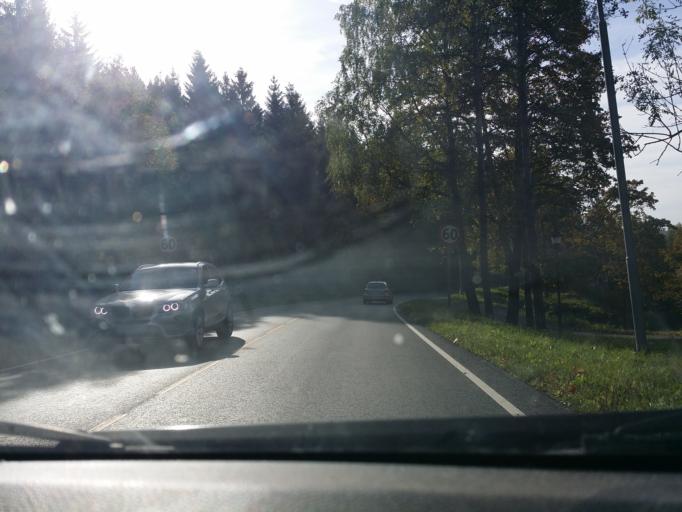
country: NO
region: Akershus
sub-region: Baerum
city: Sandvika
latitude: 59.9405
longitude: 10.5027
